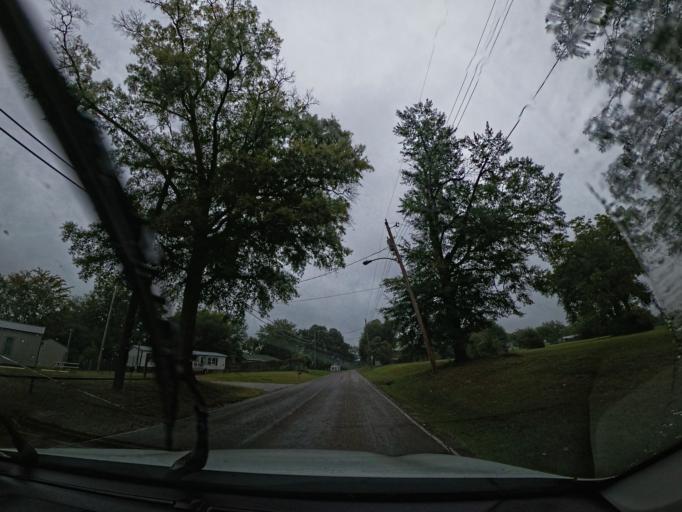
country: US
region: Texas
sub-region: Panola County
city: Carthage
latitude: 32.1542
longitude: -94.3481
